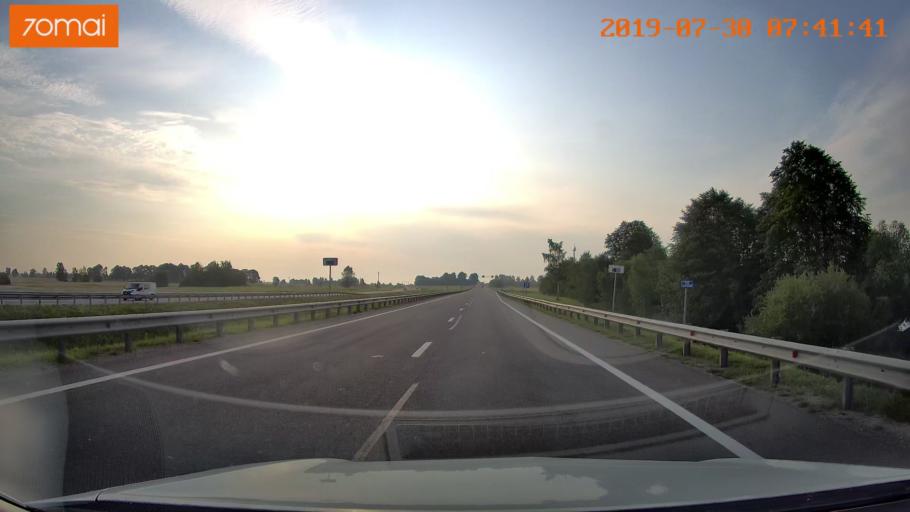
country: RU
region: Kaliningrad
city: Gvardeysk
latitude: 54.6483
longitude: 21.2583
